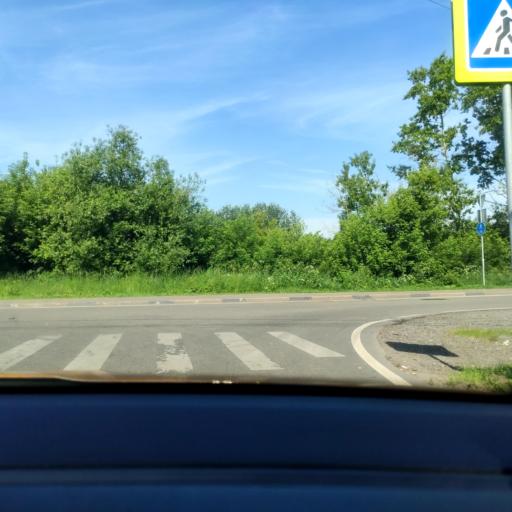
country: RU
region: Moscow
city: Vatutino
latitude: 55.8988
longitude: 37.6938
